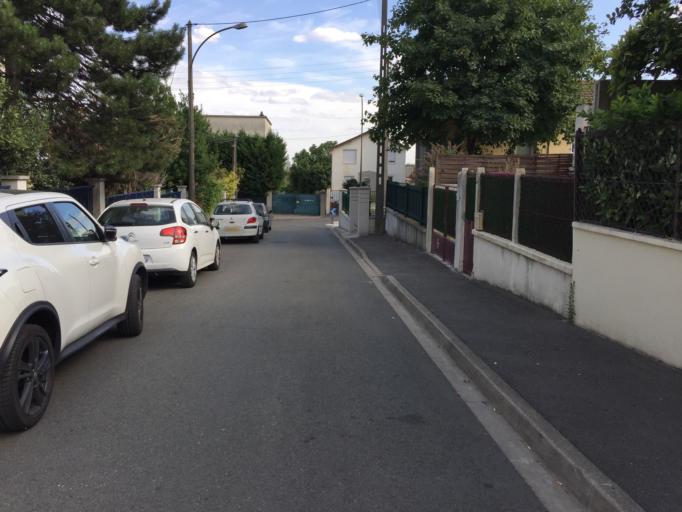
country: FR
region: Ile-de-France
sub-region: Departement du Val-d'Oise
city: Argenteuil
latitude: 48.9515
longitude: 2.2709
